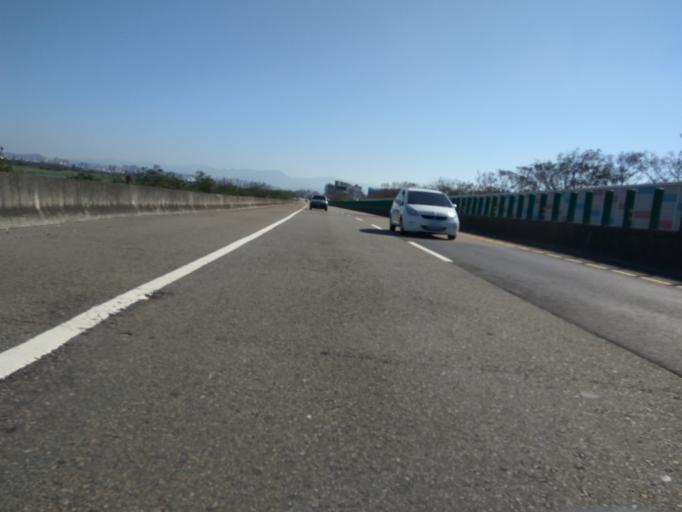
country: TW
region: Taiwan
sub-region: Hsinchu
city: Hsinchu
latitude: 24.8302
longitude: 120.9587
